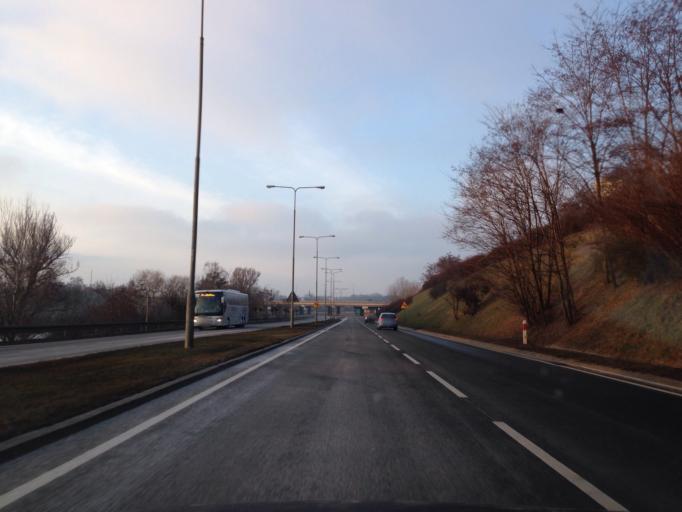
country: PL
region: Greater Poland Voivodeship
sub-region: Powiat gnieznienski
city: Gniezno
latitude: 52.5470
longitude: 17.6089
